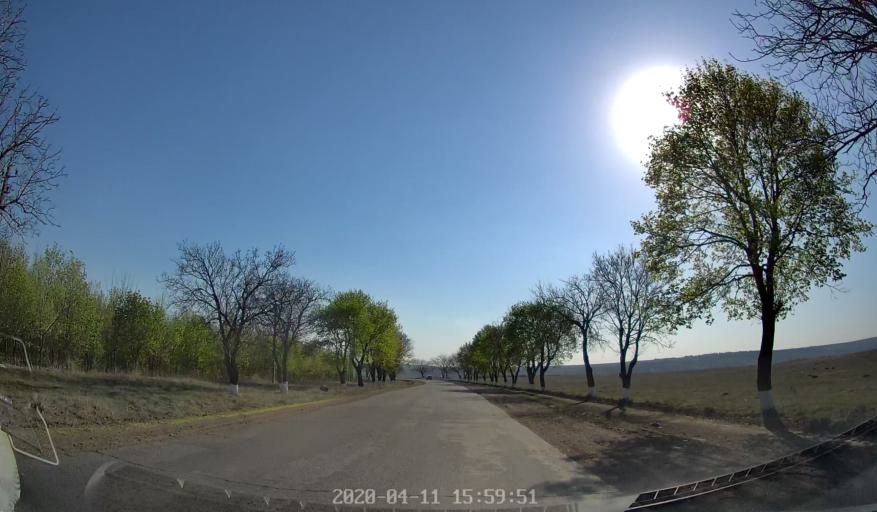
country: MD
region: Chisinau
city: Vadul lui Voda
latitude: 47.0795
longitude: 29.1378
